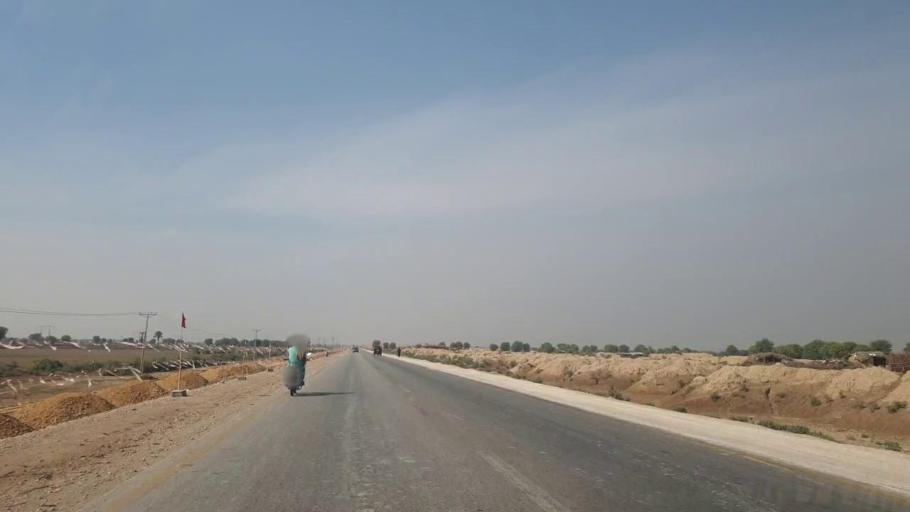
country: PK
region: Sindh
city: Sann
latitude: 25.9998
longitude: 68.1632
